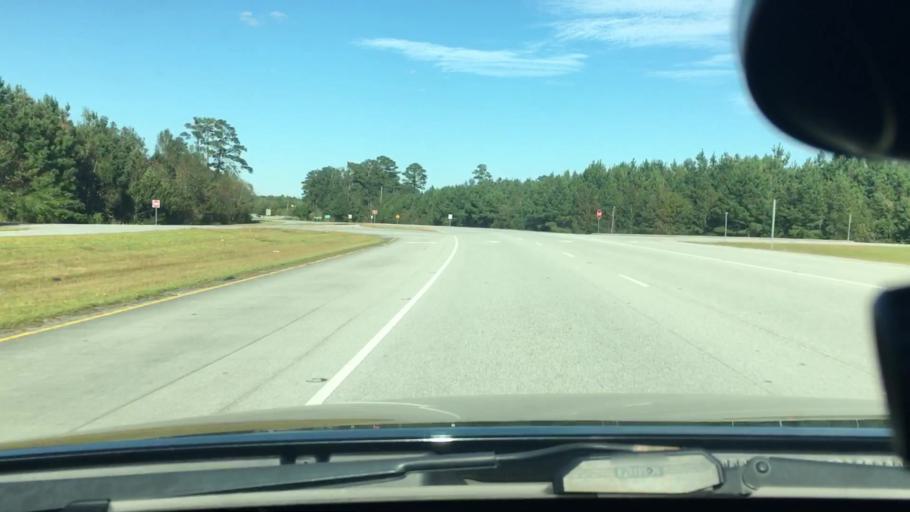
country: US
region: North Carolina
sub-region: Craven County
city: Trent Woods
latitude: 35.1400
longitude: -77.1101
